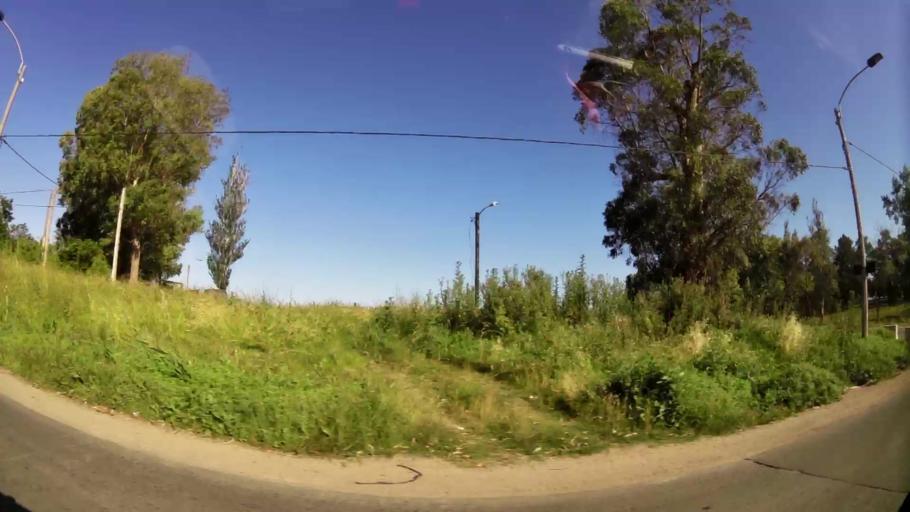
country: UY
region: Canelones
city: La Paz
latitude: -34.8088
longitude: -56.1644
